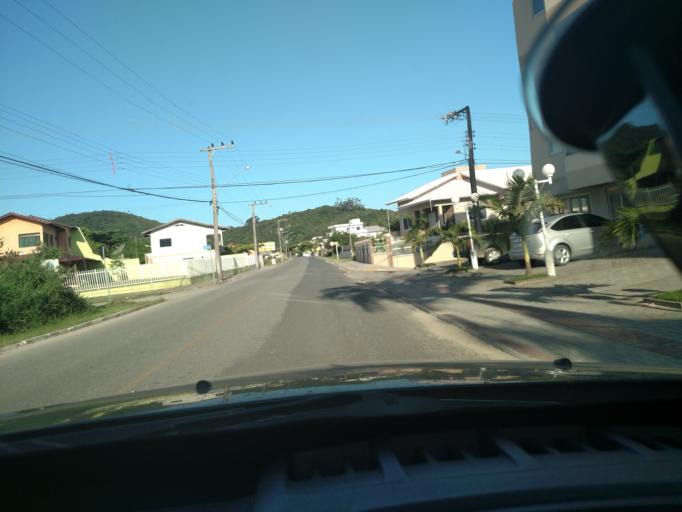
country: BR
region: Santa Catarina
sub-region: Porto Belo
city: Porto Belo
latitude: -27.1787
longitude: -48.5299
